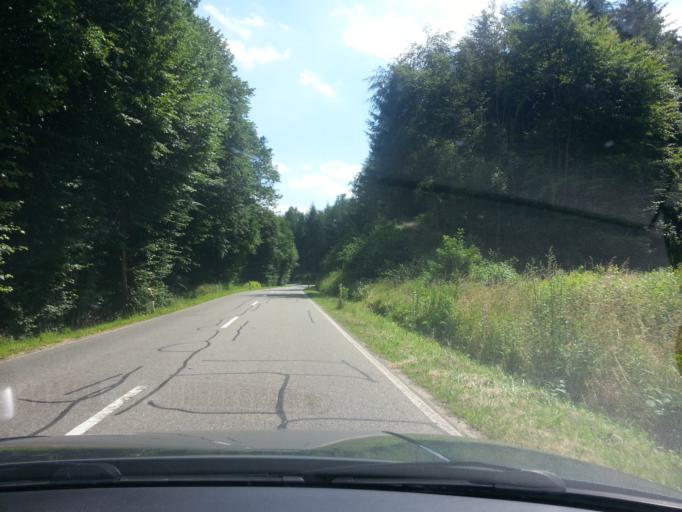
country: DE
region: Saarland
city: Spiesen-Elversberg
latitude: 49.3101
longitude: 7.1551
